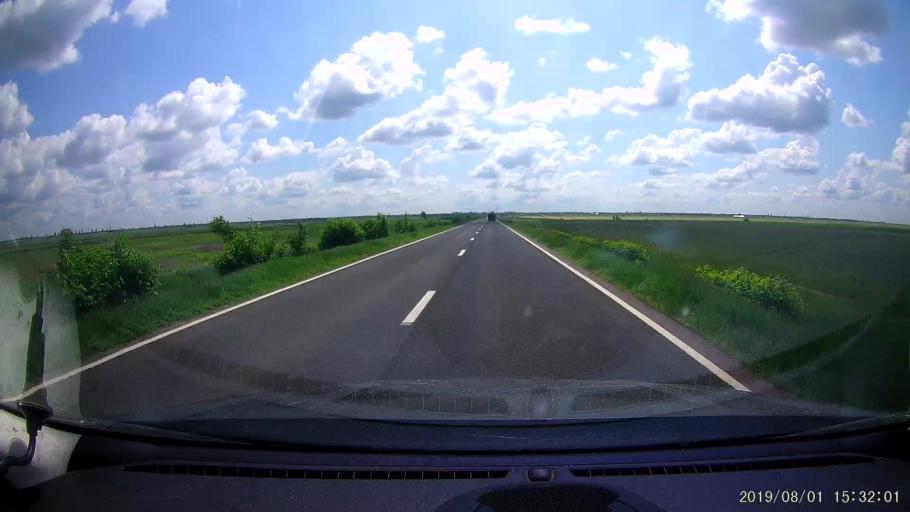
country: RO
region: Braila
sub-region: Comuna Insuratei
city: Insuratei
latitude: 44.9370
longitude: 27.6461
